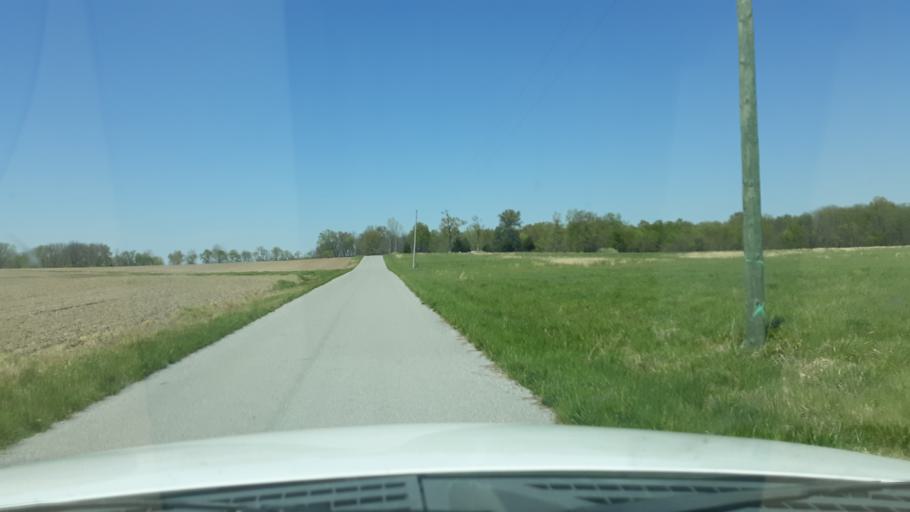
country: US
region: Illinois
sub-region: Saline County
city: Harrisburg
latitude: 37.8895
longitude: -88.6698
